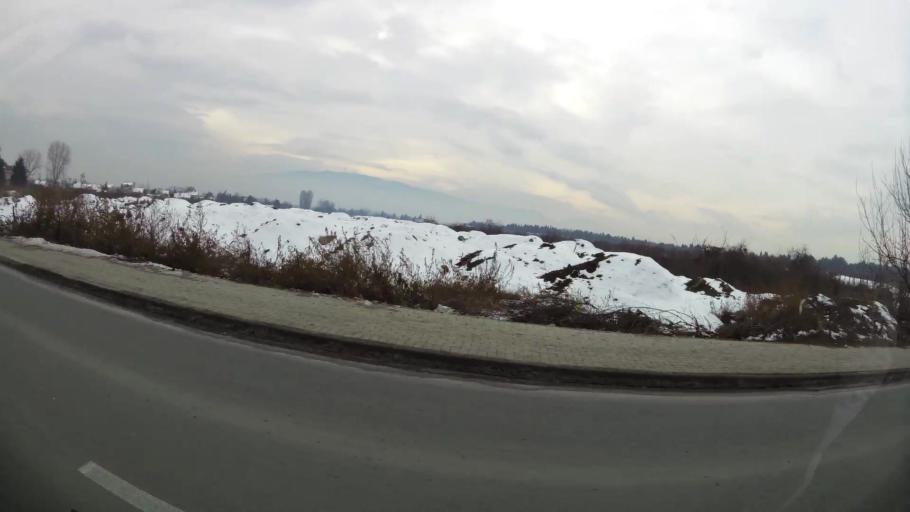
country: MK
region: Butel
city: Butel
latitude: 42.0376
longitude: 21.4421
